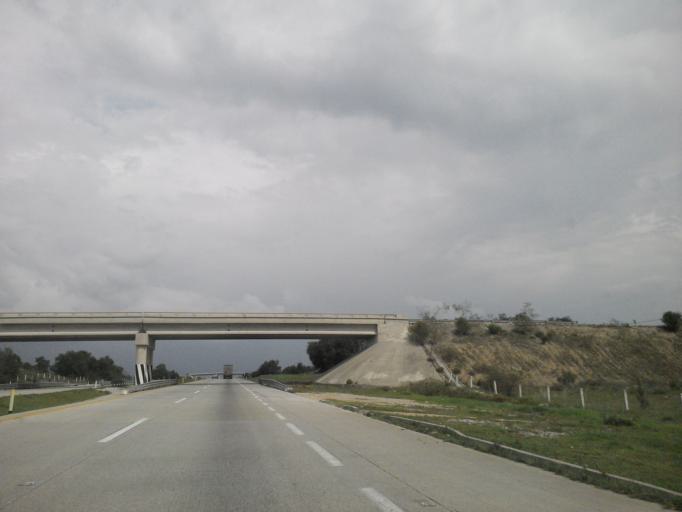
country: MX
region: Mexico
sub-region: Apaxco
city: Colonia Juarez
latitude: 19.9904
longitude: -99.1296
